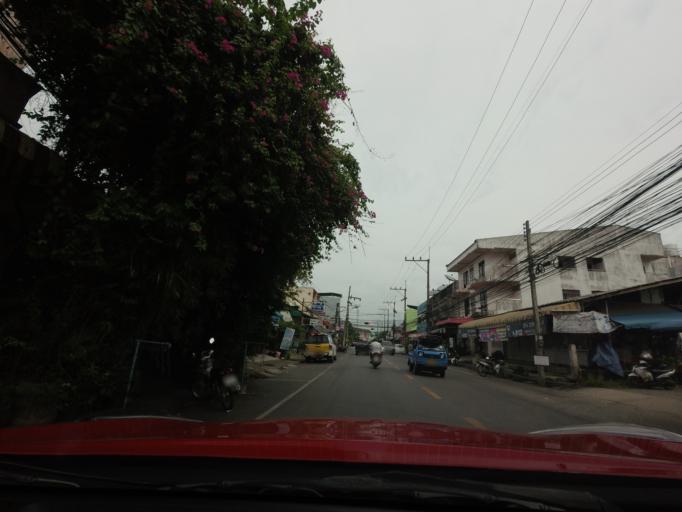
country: TH
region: Songkhla
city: Hat Yai
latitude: 6.9936
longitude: 100.4762
